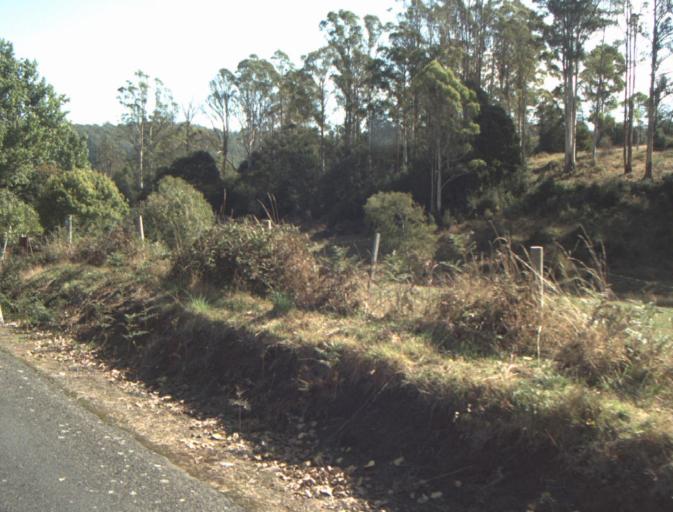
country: AU
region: Tasmania
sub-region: Launceston
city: Mayfield
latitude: -41.2884
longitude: 147.2102
